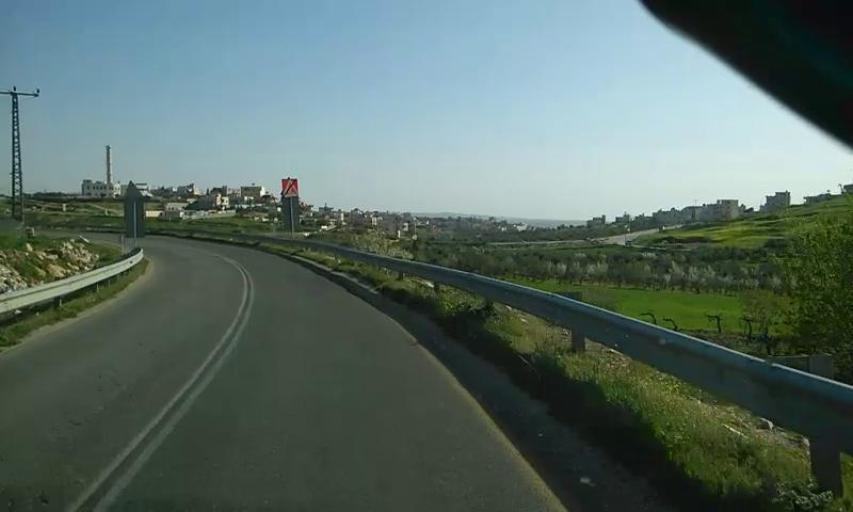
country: PS
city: Al Hilah
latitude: 31.4721
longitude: 35.1328
